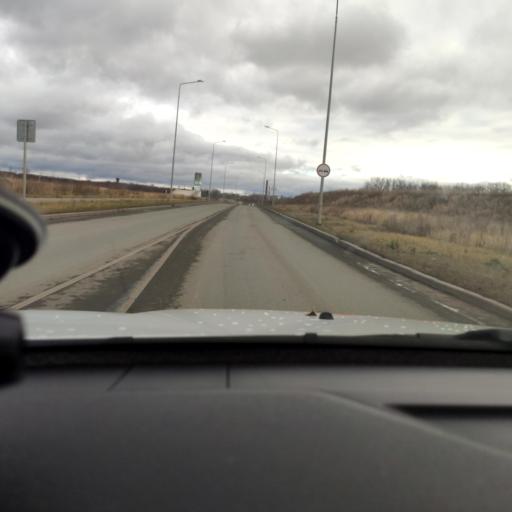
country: RU
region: Samara
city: Petra-Dubrava
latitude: 53.3106
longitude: 50.3461
